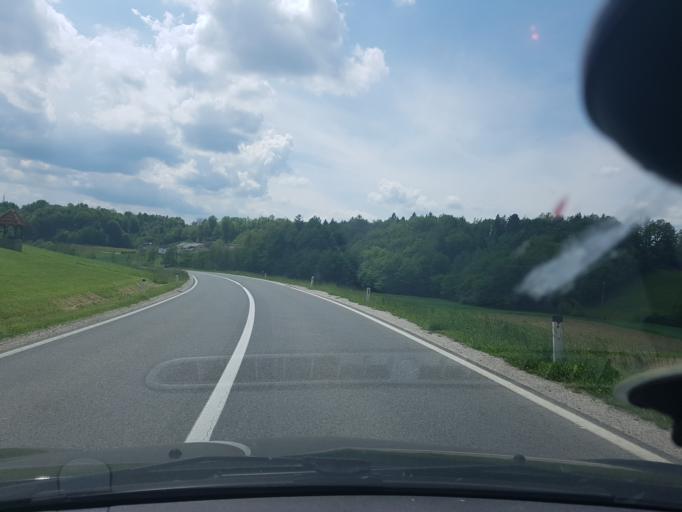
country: SI
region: Rogaska Slatina
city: Rogaska Slatina
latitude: 46.2507
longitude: 15.6054
